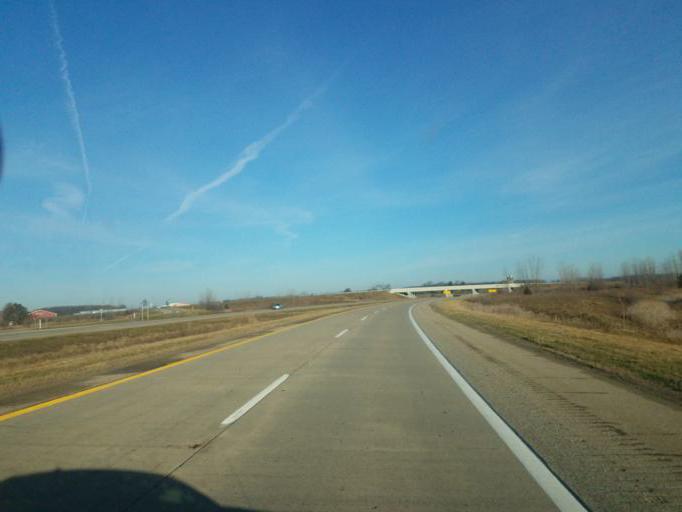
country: US
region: Michigan
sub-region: Clinton County
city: Saint Johns
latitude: 43.0262
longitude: -84.5584
